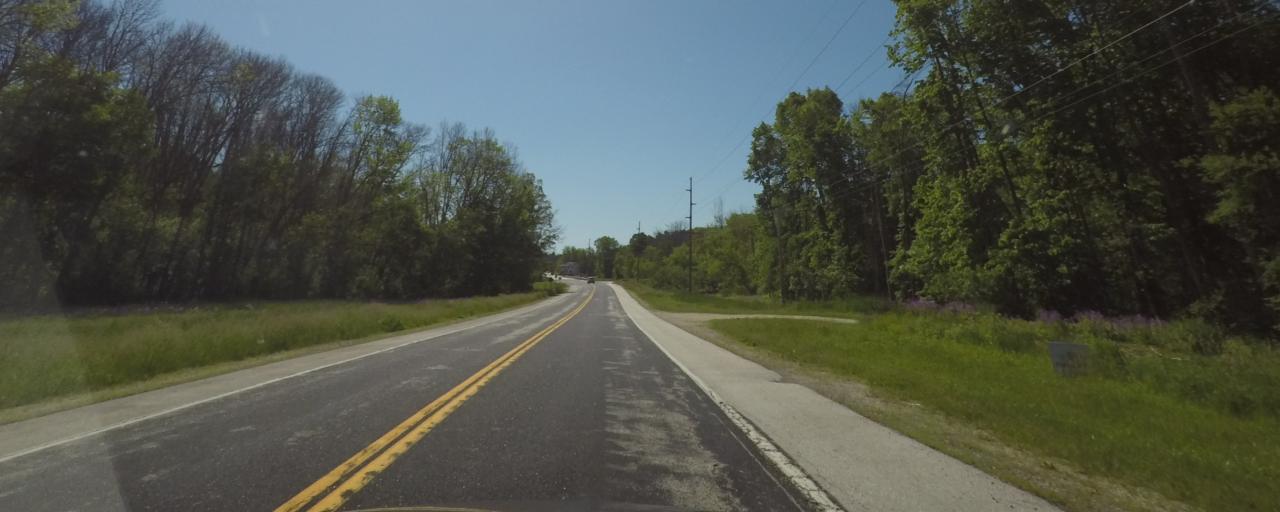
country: US
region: Wisconsin
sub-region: Sheboygan County
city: Sheboygan Falls
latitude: 43.7378
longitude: -87.8442
